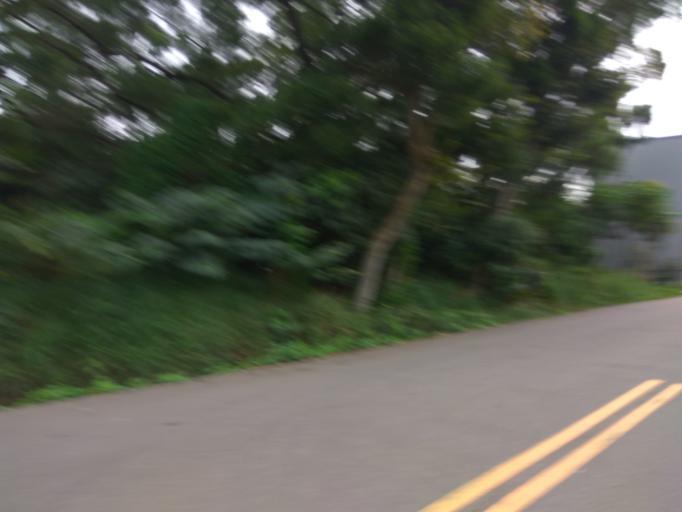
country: TW
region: Taiwan
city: Taoyuan City
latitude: 24.9874
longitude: 121.2284
